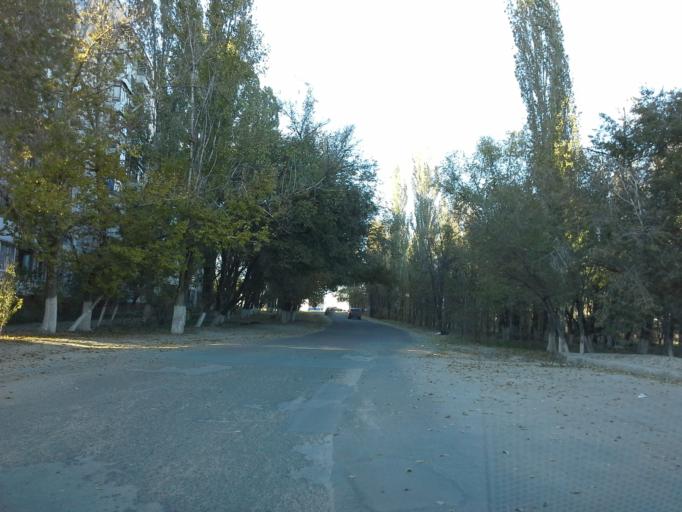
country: RU
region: Volgograd
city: Vodstroy
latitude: 48.8239
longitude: 44.6400
